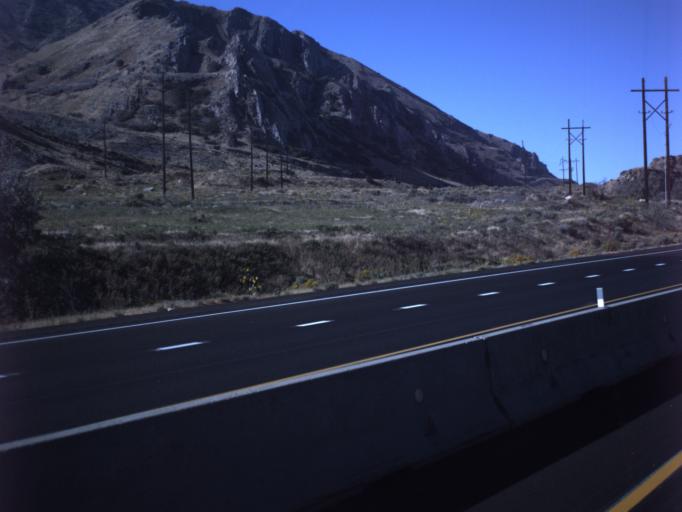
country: US
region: Utah
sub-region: Tooele County
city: Stansbury park
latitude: 40.7224
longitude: -112.2192
